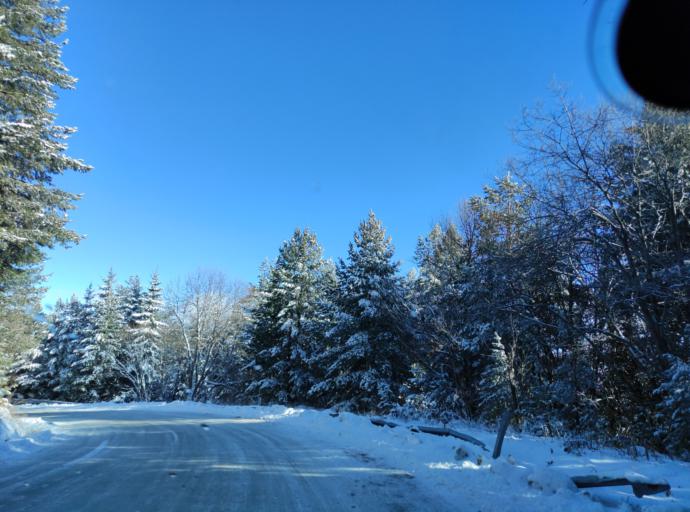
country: BG
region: Sofia-Capital
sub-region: Stolichna Obshtina
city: Sofia
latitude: 42.5902
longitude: 23.2961
